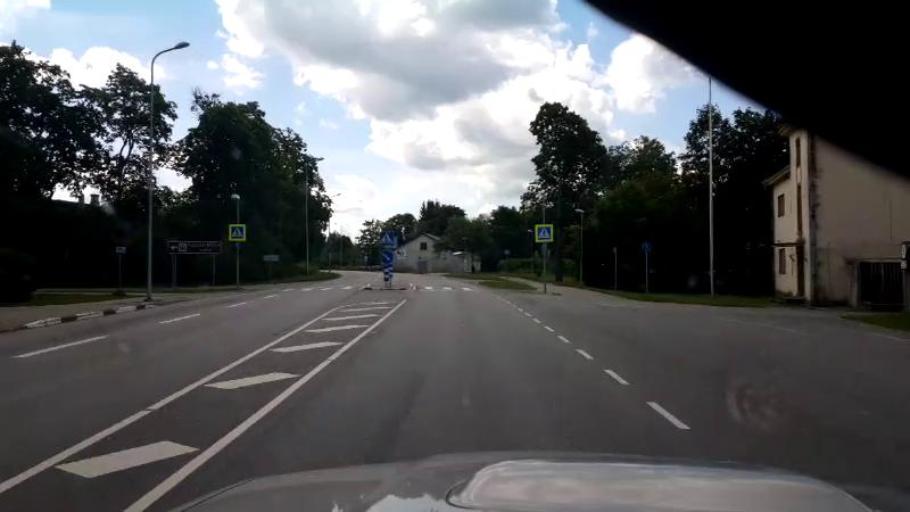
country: EE
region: Jaervamaa
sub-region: Jaerva-Jaani vald
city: Jarva-Jaani
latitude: 59.0298
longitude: 25.7027
